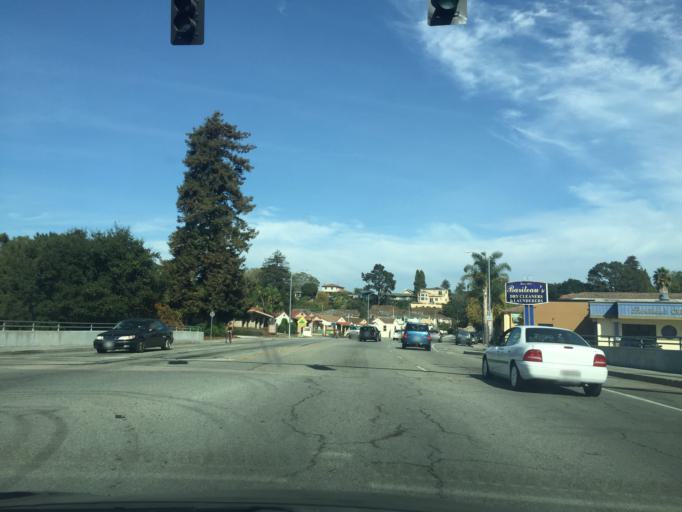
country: US
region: California
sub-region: Santa Cruz County
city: Santa Cruz
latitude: 36.9803
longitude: -122.0191
